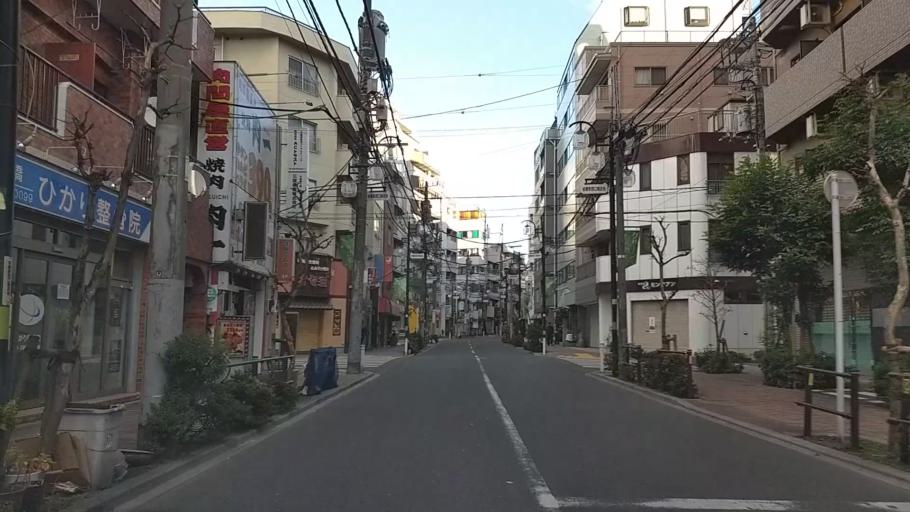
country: JP
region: Saitama
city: Kawaguchi
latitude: 35.7467
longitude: 139.7178
